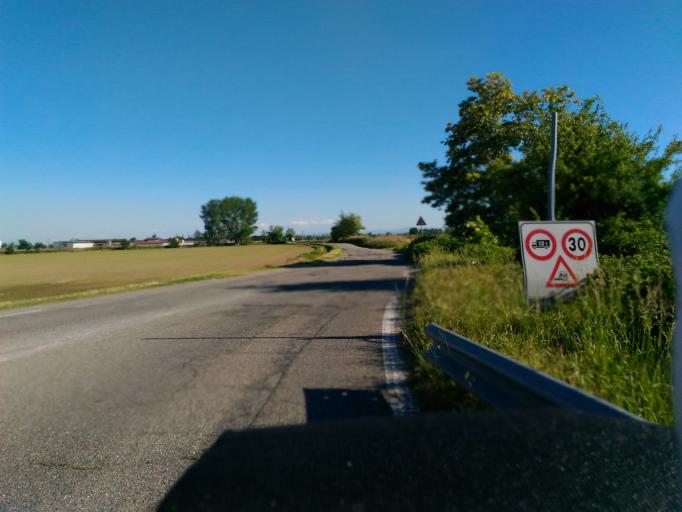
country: IT
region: Lombardy
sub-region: Citta metropolitana di Milano
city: Locate di Triulzi
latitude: 45.3650
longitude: 9.2481
